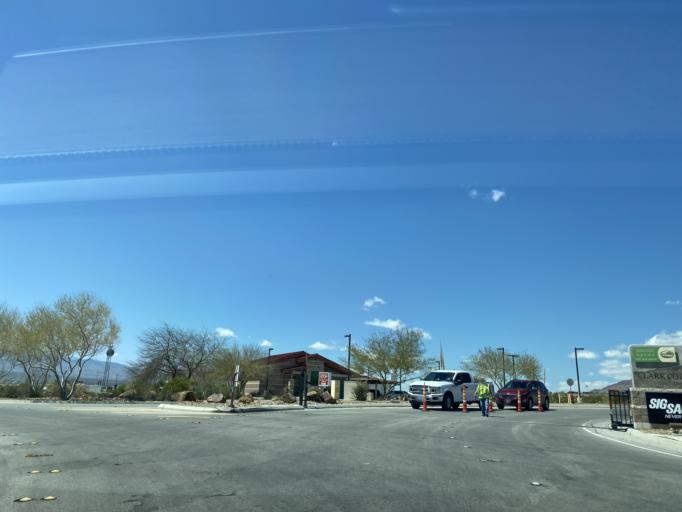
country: US
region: Nevada
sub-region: Clark County
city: North Las Vegas
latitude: 36.3361
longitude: -115.2078
